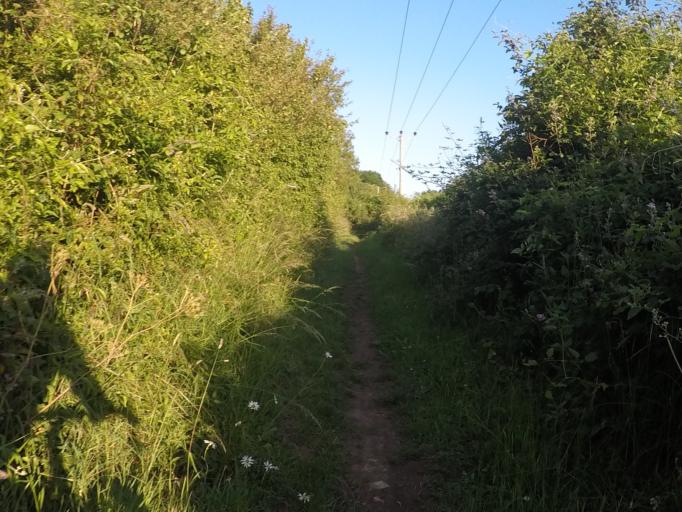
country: GB
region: England
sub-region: Oxfordshire
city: Charlbury
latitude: 51.8938
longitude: -1.4643
